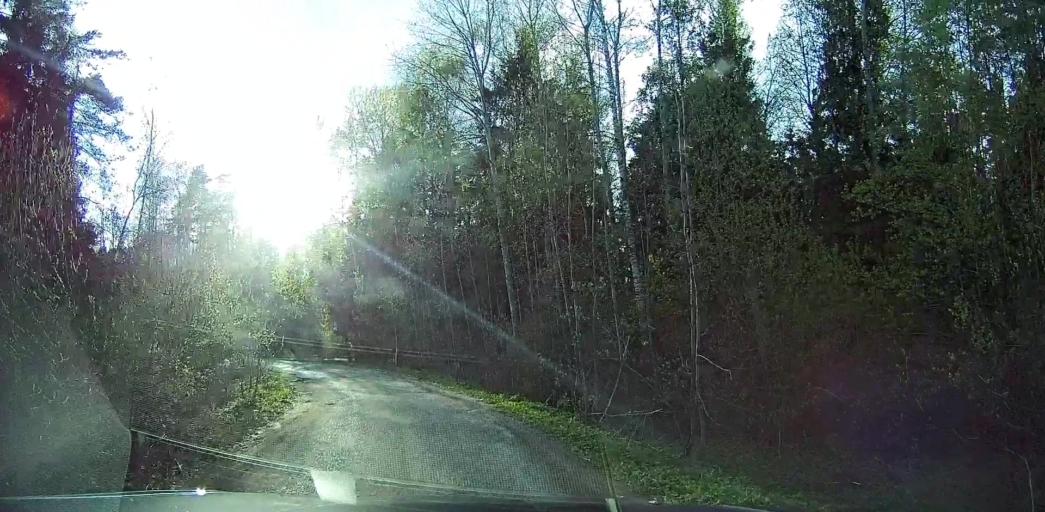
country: RU
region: Moskovskaya
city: Malyshevo
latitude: 55.5543
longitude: 38.3393
